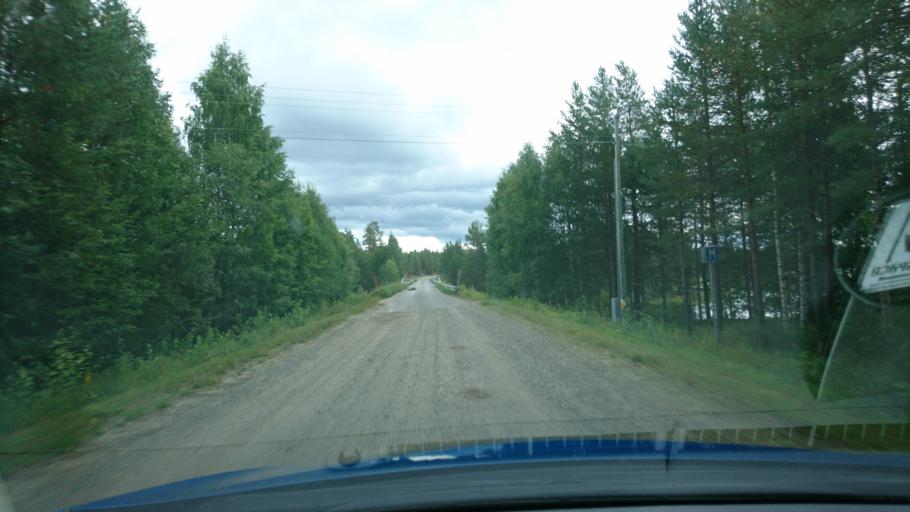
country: SE
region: Vaesterbotten
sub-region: Norsjo Kommun
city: Norsjoe
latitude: 64.5032
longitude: 19.2627
